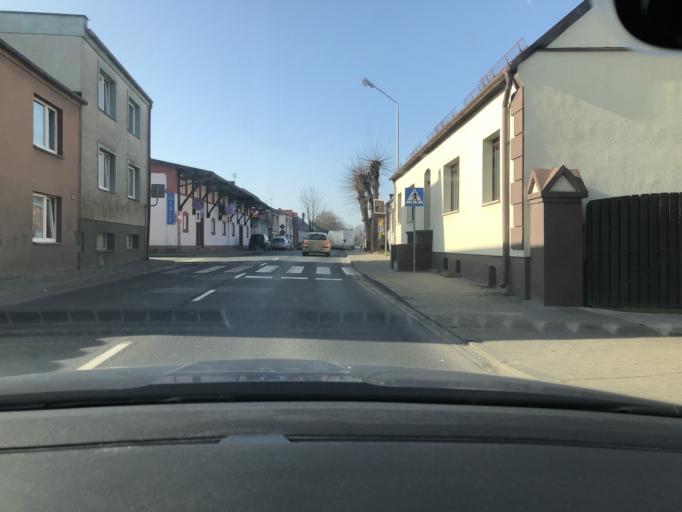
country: PL
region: Greater Poland Voivodeship
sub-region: Powiat poznanski
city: Buk
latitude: 52.3589
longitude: 16.5176
